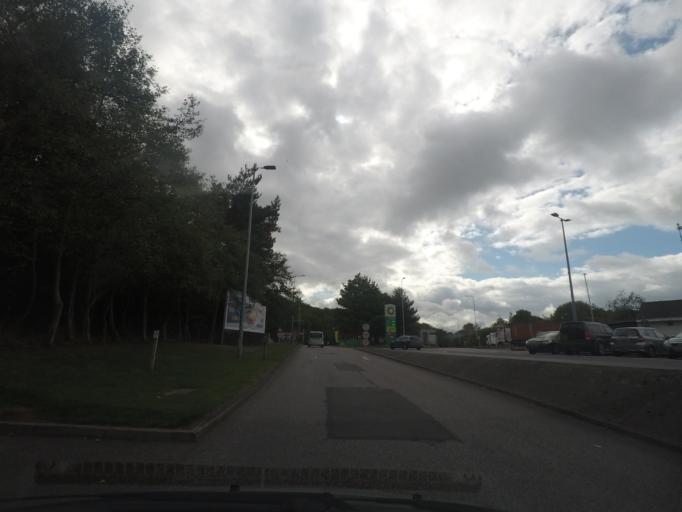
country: GB
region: England
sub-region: City and Borough of Wakefield
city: Crigglestone
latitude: 53.6212
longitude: -1.5456
